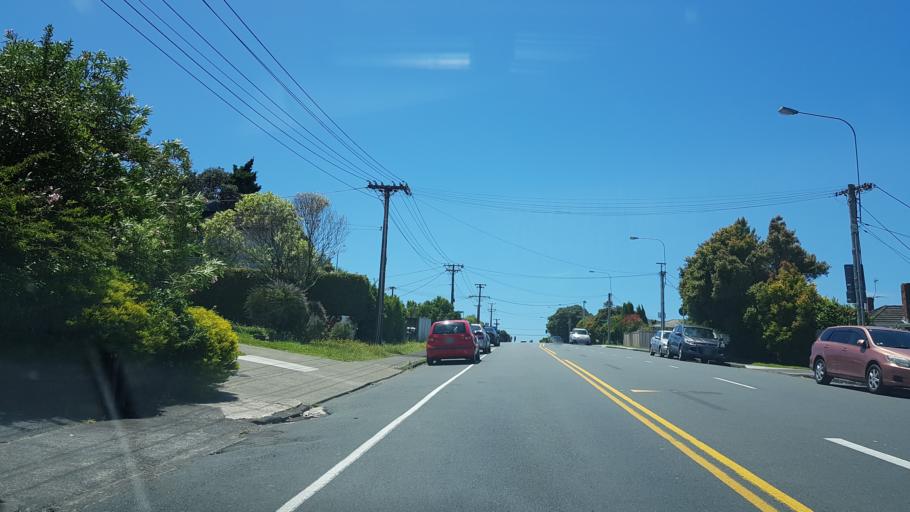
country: NZ
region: Auckland
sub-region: Auckland
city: North Shore
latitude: -36.7707
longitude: 174.7469
